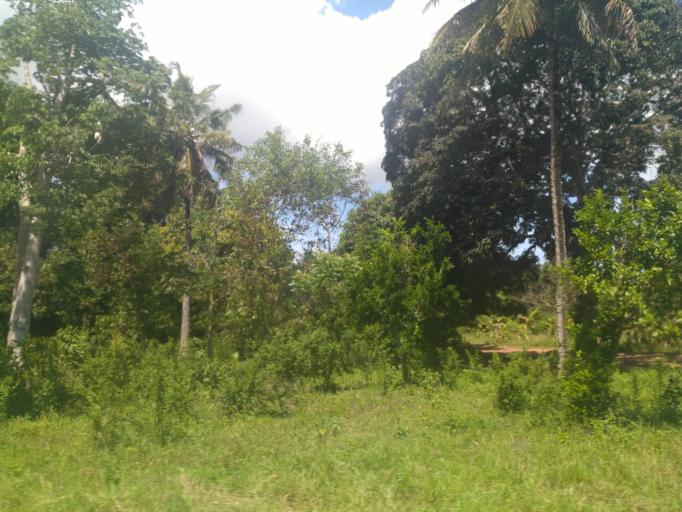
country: TZ
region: Zanzibar North
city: Gamba
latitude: -5.9310
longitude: 39.3411
